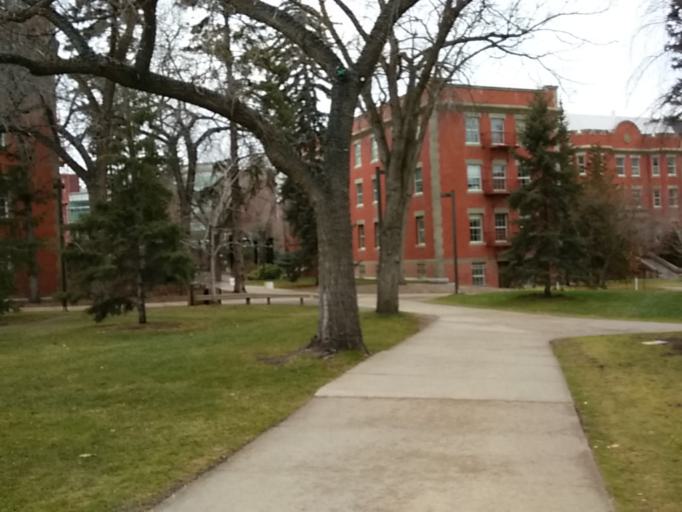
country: CA
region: Alberta
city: Edmonton
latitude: 53.5270
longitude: -113.5258
